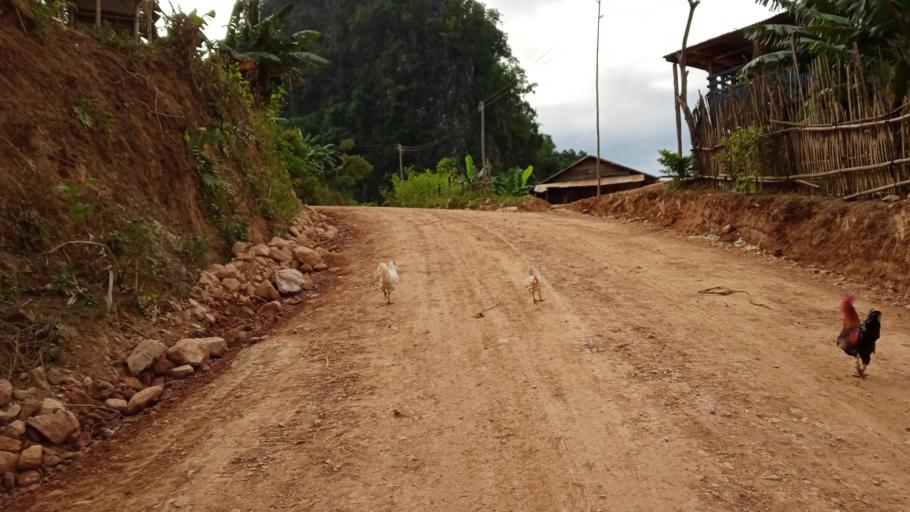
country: LA
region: Xiangkhoang
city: Phonsavan
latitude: 19.1187
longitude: 102.9151
